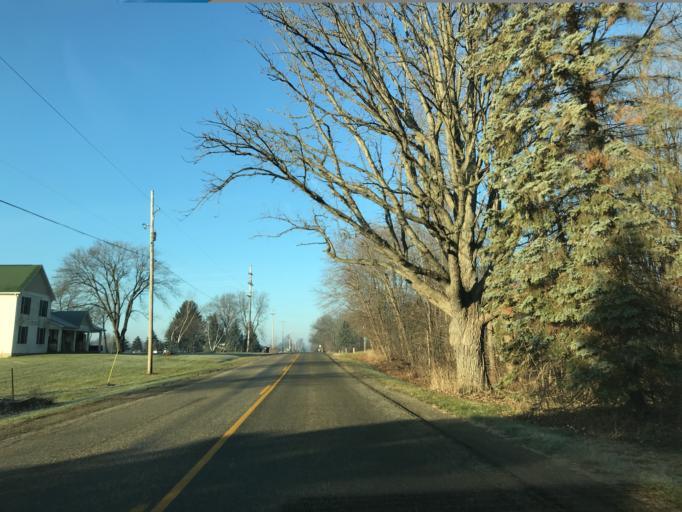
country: US
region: Michigan
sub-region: Eaton County
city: Dimondale
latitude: 42.6620
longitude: -84.6210
